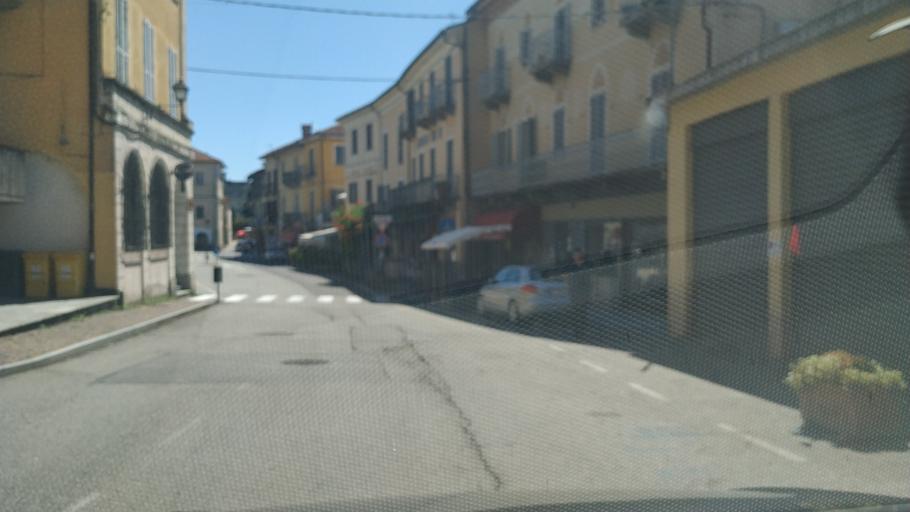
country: IT
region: Piedmont
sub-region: Provincia di Torino
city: Castellamonte
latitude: 45.3836
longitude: 7.7097
